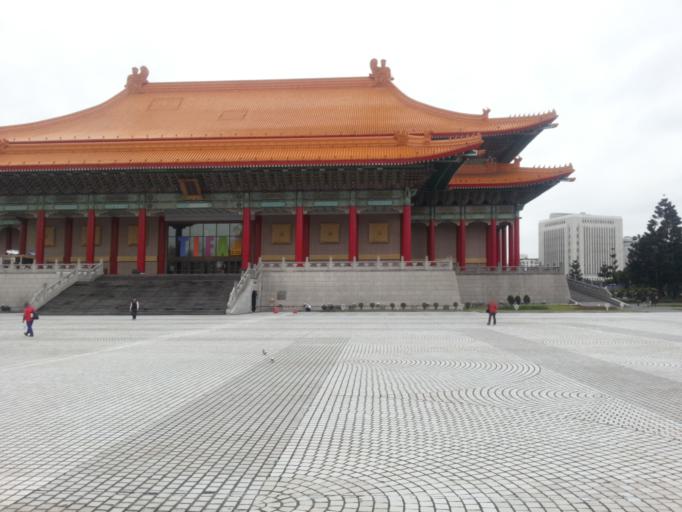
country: TW
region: Taipei
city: Taipei
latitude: 25.0363
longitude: 121.5185
